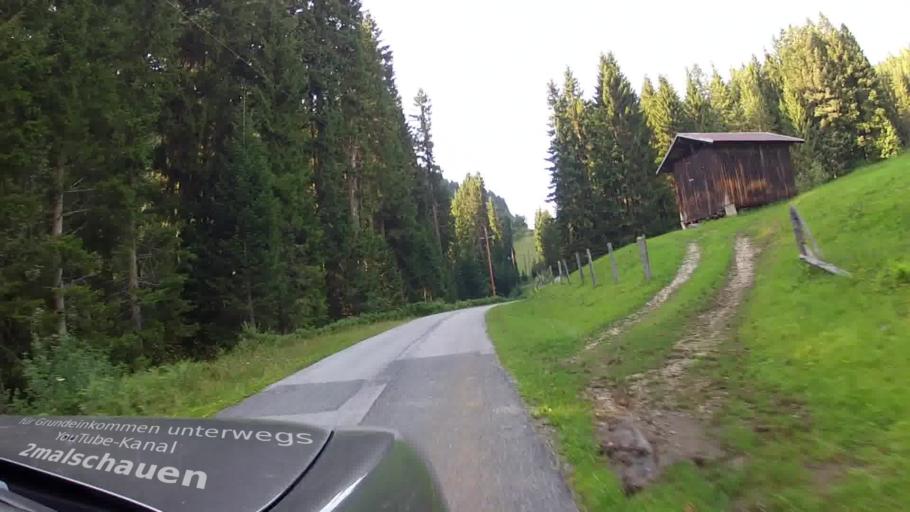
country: AT
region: Salzburg
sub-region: Politischer Bezirk Sankt Johann im Pongau
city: Eben im Pongau
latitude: 47.4336
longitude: 13.3806
